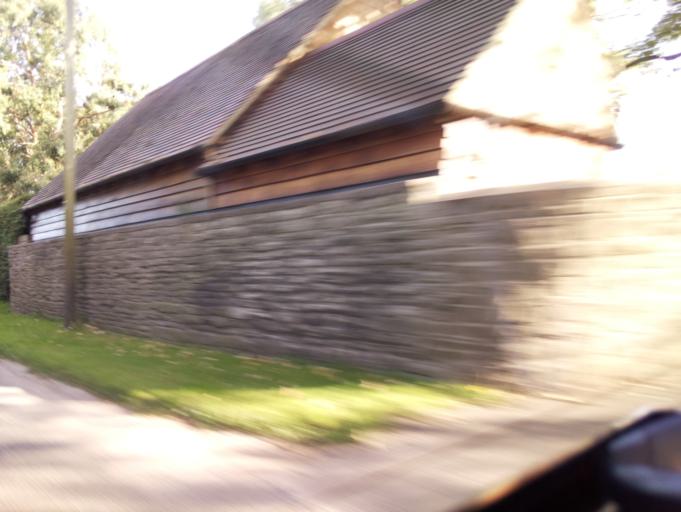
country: GB
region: England
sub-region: Gloucestershire
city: Gloucester
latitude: 51.9626
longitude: -2.2978
